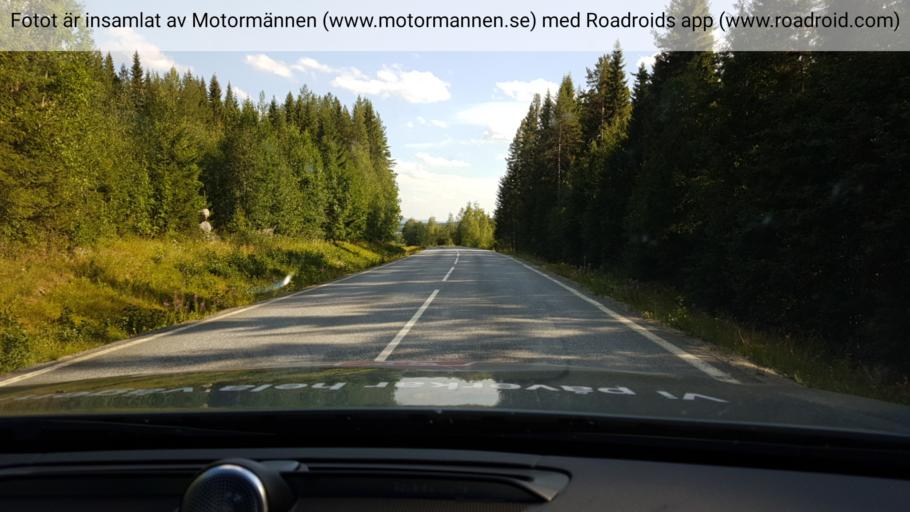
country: SE
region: Vaesterbotten
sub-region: Dorotea Kommun
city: Dorotea
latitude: 63.8633
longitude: 16.3858
